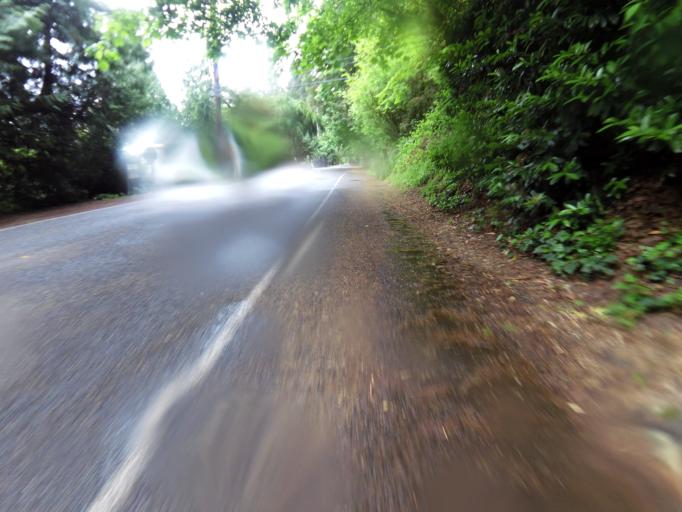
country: US
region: Washington
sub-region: King County
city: Mercer Island
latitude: 47.5424
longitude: -122.2129
